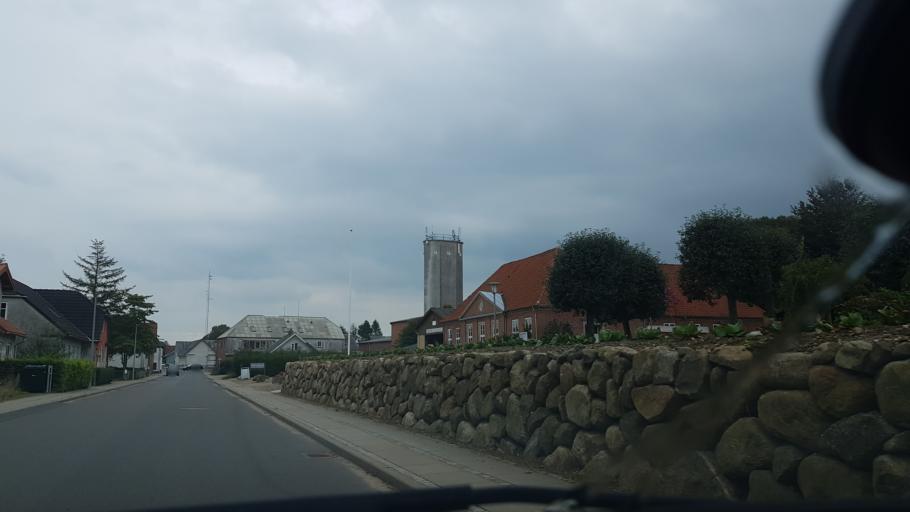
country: DK
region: South Denmark
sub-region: Vejle Kommune
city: Egtved
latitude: 55.5590
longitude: 9.3090
